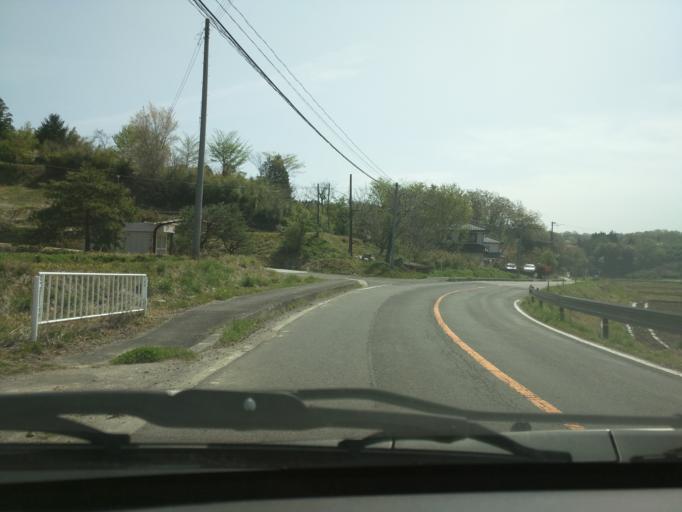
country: JP
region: Fukushima
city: Nihommatsu
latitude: 37.5726
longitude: 140.4710
